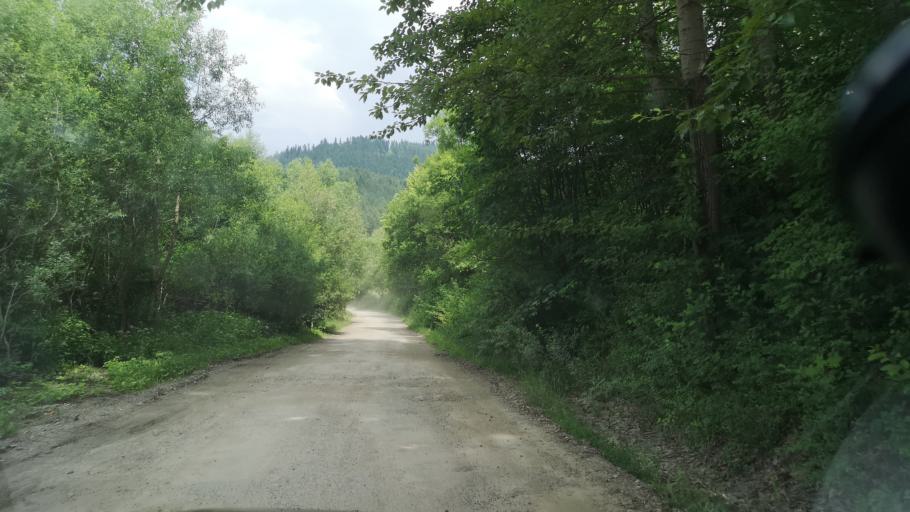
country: SK
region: Zilinsky
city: Ruzomberok
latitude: 49.1304
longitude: 19.4188
